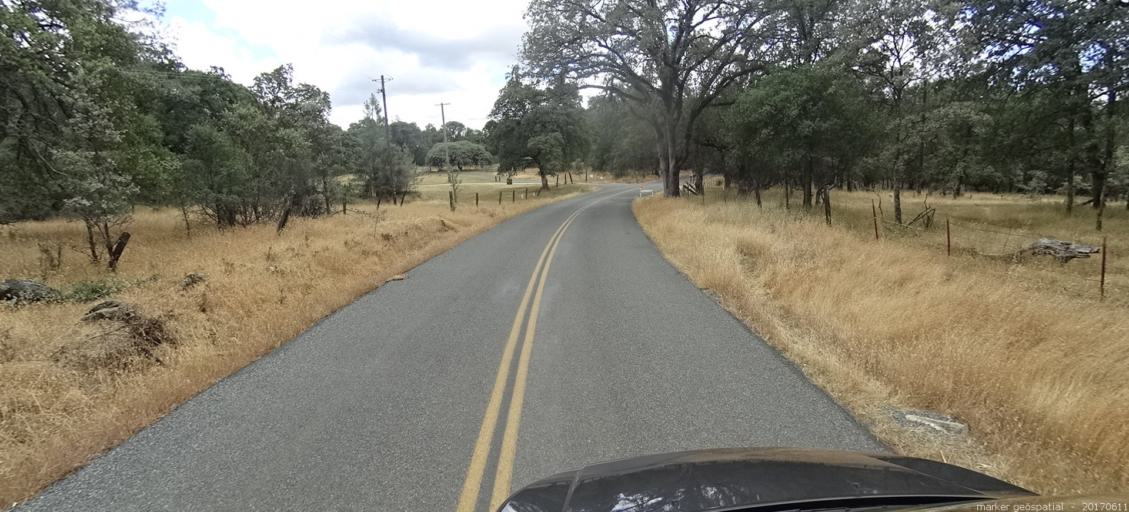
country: US
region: California
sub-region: Butte County
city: Oroville
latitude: 39.6117
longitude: -121.5269
